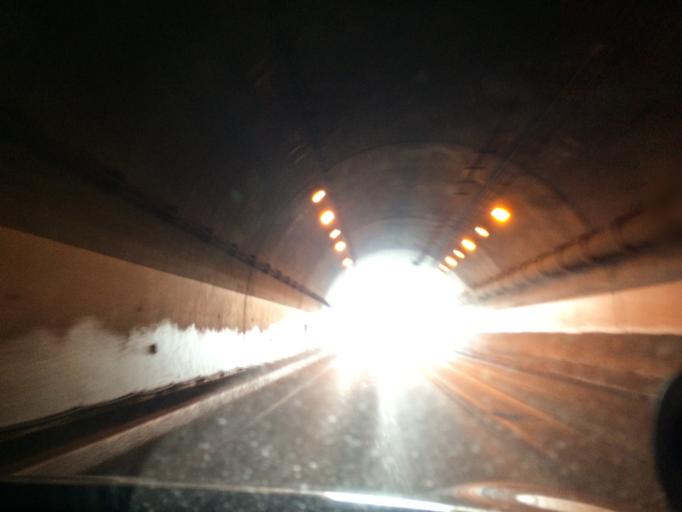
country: JP
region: Hokkaido
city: Shimo-furano
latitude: 42.8934
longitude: 142.3047
